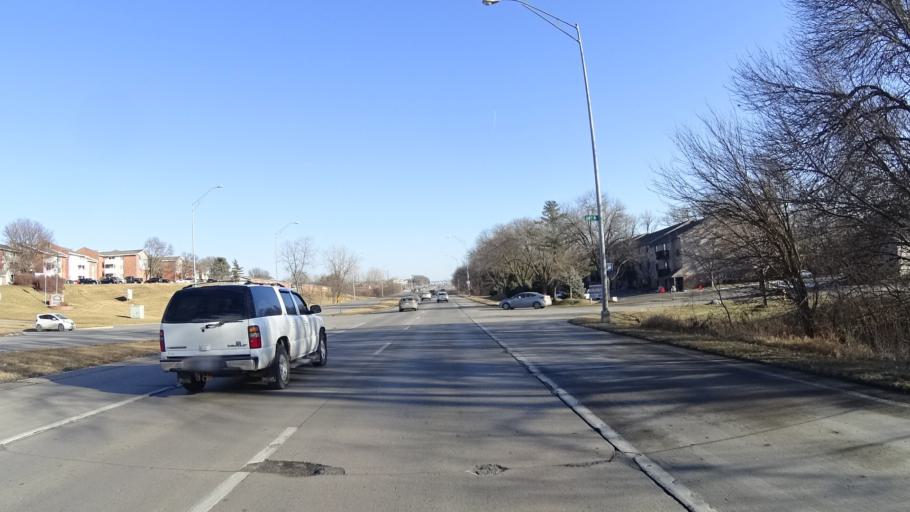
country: US
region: Nebraska
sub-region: Douglas County
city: Bennington
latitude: 41.2902
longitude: -96.0931
